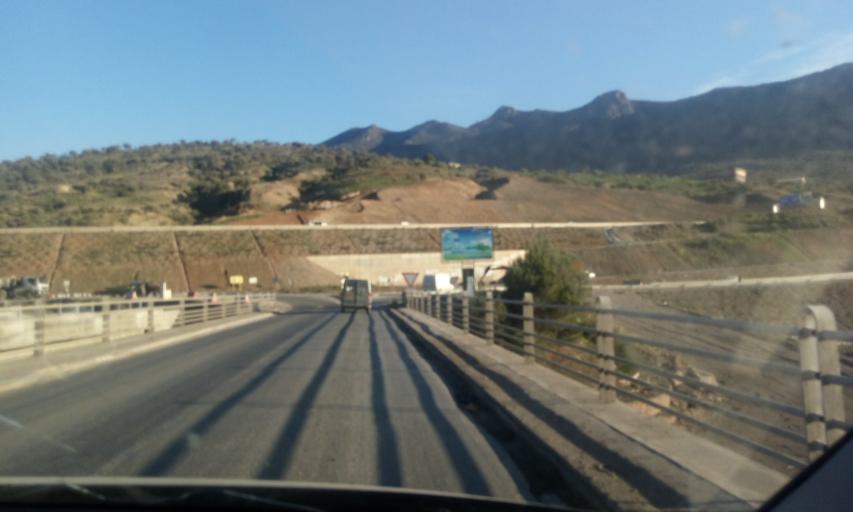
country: DZ
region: Bejaia
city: Akbou
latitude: 36.4804
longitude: 4.5934
